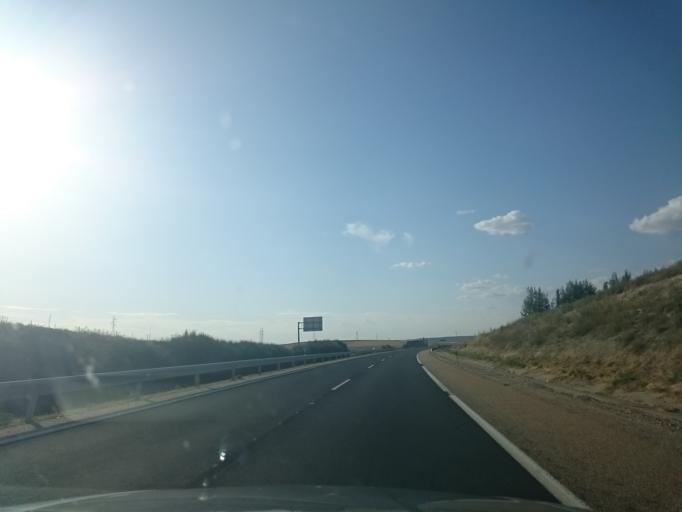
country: ES
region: Castille and Leon
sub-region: Provincia de Burgos
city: Villagonzalo-Pedernales
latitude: 42.3143
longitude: -3.7607
